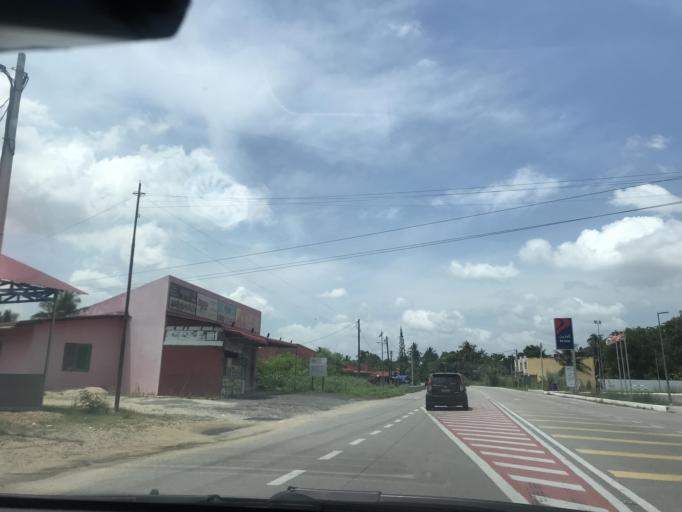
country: MY
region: Kelantan
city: Kota Bharu
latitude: 6.1552
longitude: 102.2027
